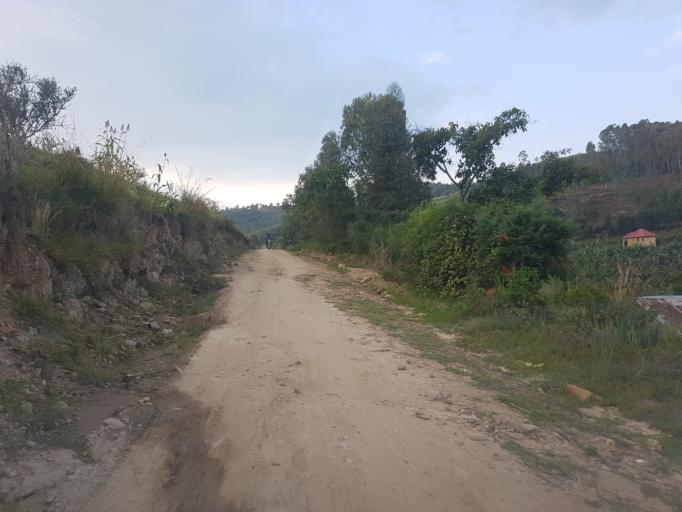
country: UG
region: Western Region
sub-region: Mitoma District
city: Mitoma
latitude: -0.6818
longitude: 29.9112
